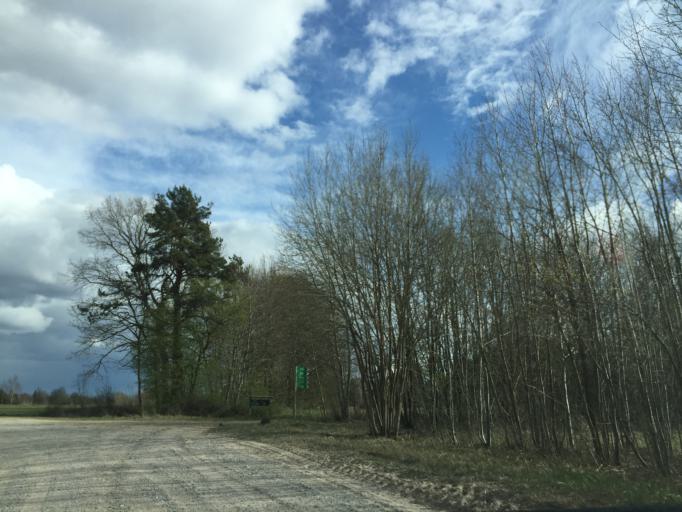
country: LV
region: Burtnieki
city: Matisi
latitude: 57.6239
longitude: 25.0624
